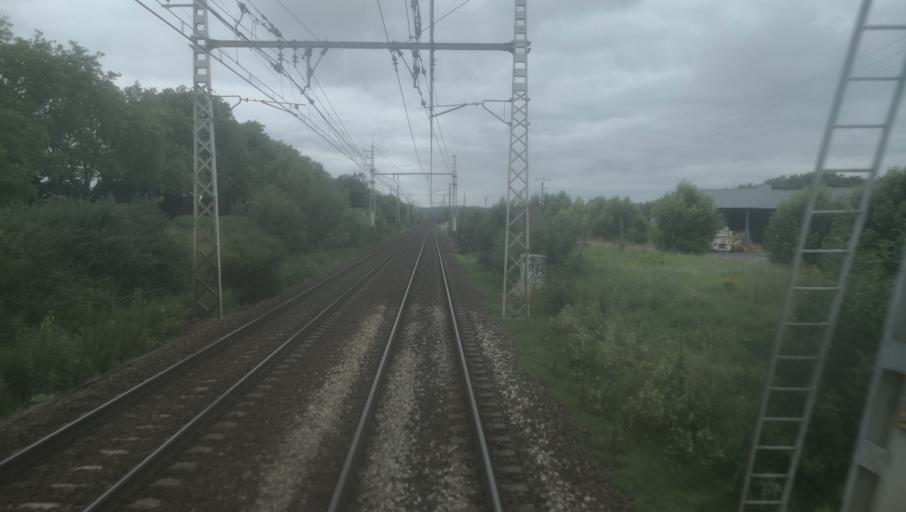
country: FR
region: Midi-Pyrenees
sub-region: Departement de la Haute-Garonne
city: Saint-Jory
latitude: 43.7463
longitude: 1.3650
